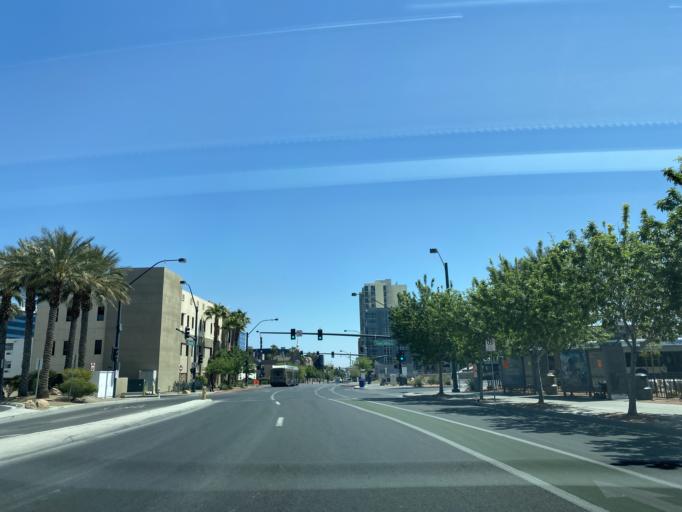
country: US
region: Nevada
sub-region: Clark County
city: Las Vegas
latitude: 36.1653
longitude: -115.1490
